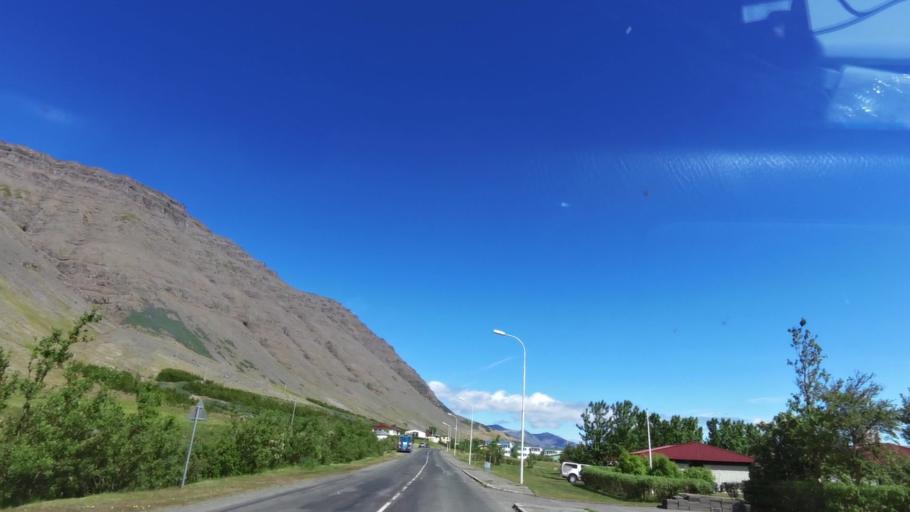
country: IS
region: Westfjords
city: Isafjoerdur
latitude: 65.6778
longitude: -23.6122
